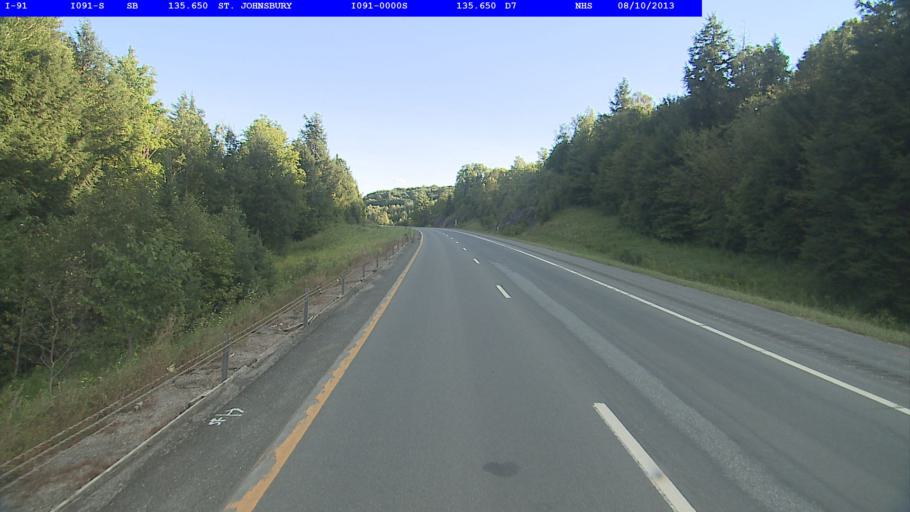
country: US
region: Vermont
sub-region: Caledonia County
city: Lyndon
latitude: 44.4987
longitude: -72.0217
